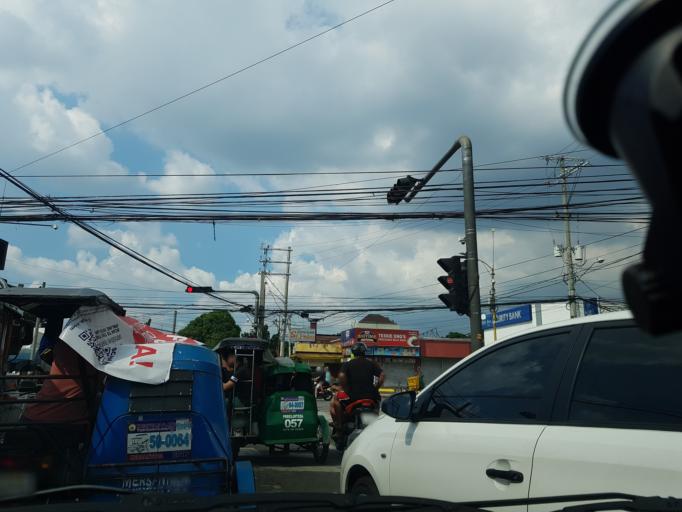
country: PH
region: Metro Manila
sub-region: Pasig
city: Pasig City
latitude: 14.5682
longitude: 121.0860
